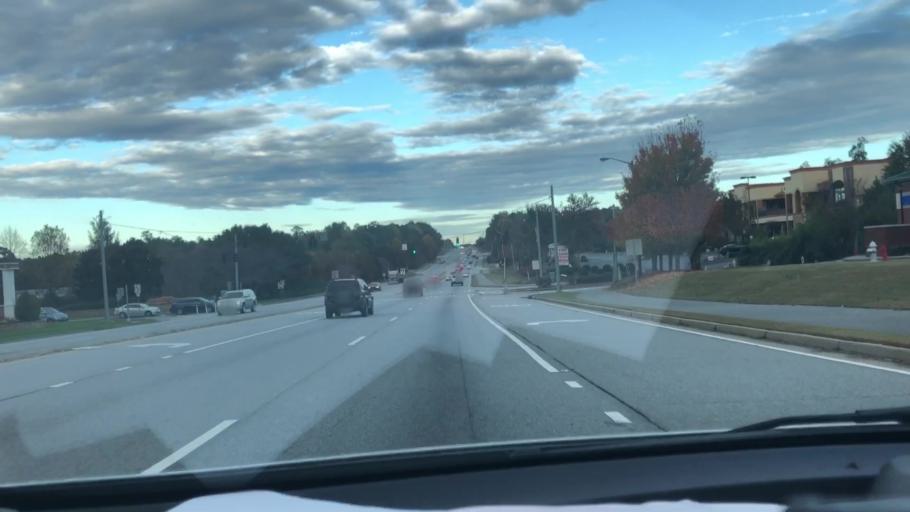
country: US
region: Georgia
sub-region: Gwinnett County
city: Berkeley Lake
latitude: 33.9692
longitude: -84.1928
